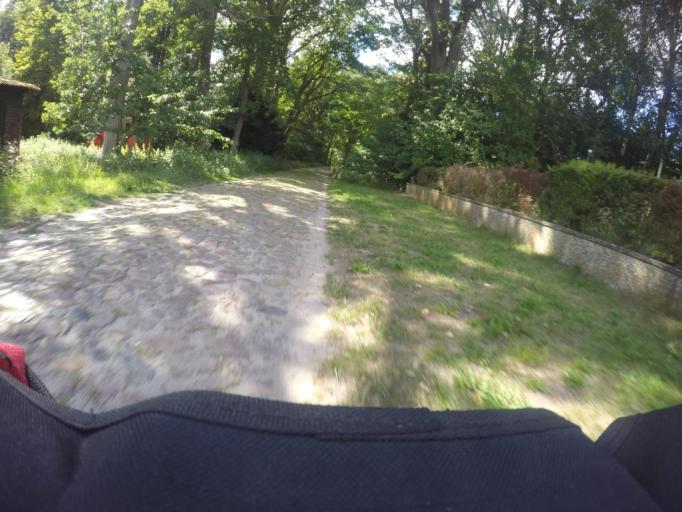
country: DE
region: Lower Saxony
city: Thomasburg
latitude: 53.2242
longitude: 10.6707
